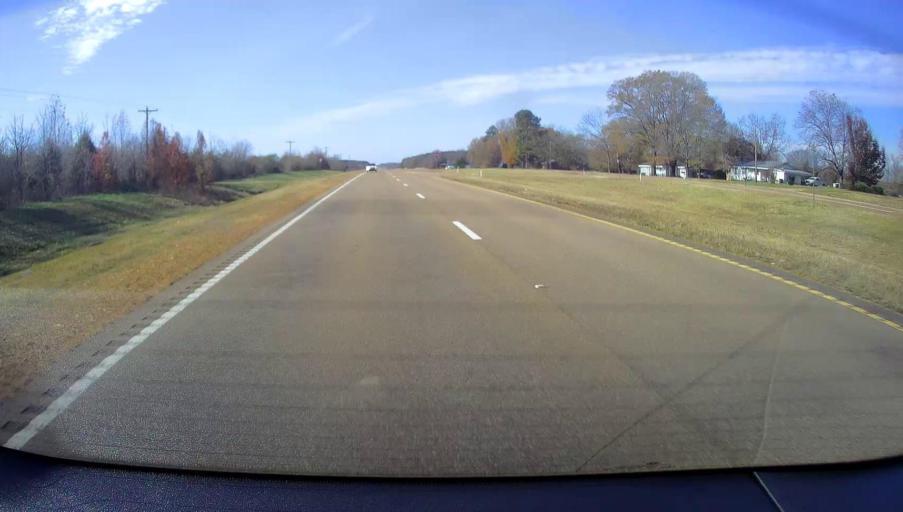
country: US
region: Mississippi
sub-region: Benton County
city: Ashland
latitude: 34.9461
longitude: -89.2044
